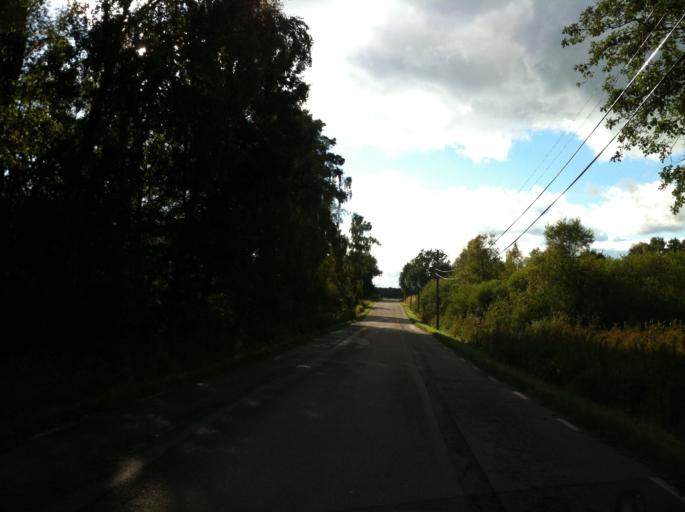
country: SE
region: Skane
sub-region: Perstorps Kommun
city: Perstorp
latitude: 56.0458
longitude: 13.3782
